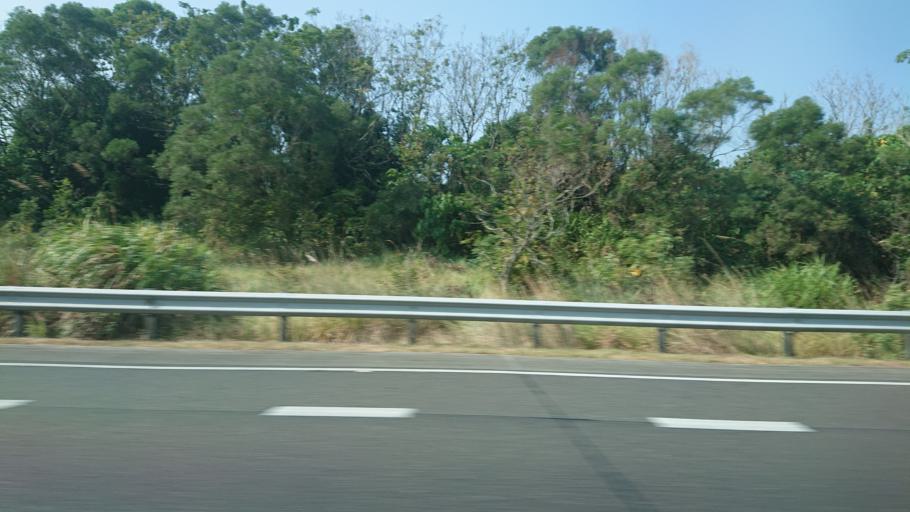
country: TW
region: Taiwan
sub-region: Nantou
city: Nantou
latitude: 23.8404
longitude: 120.7055
